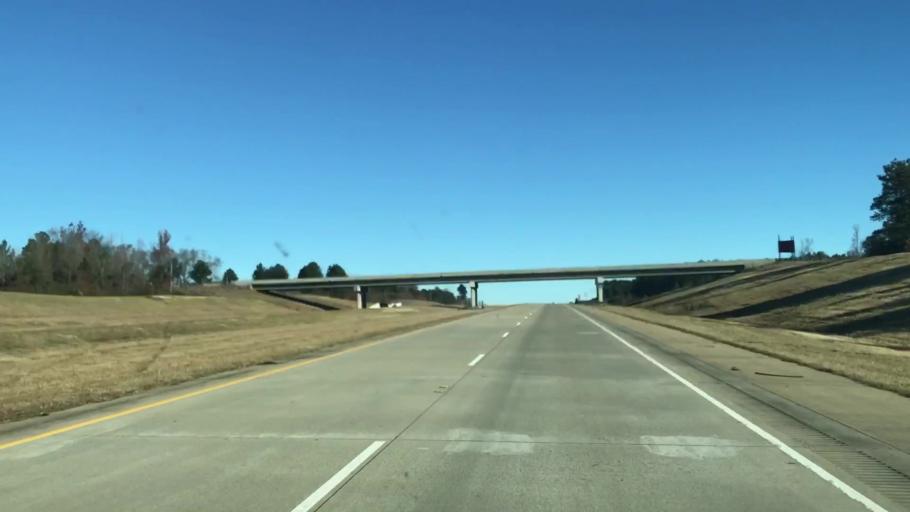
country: US
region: Louisiana
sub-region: Caddo Parish
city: Vivian
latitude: 33.0061
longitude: -93.9057
